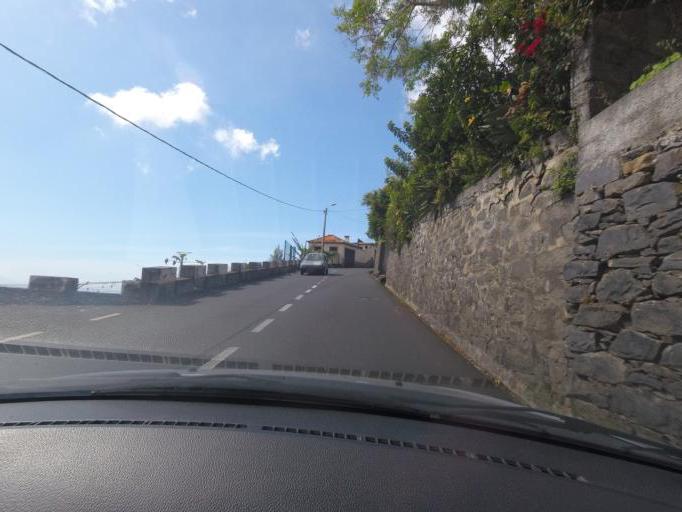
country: PT
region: Madeira
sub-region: Funchal
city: Nossa Senhora do Monte
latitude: 32.6716
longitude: -16.9374
